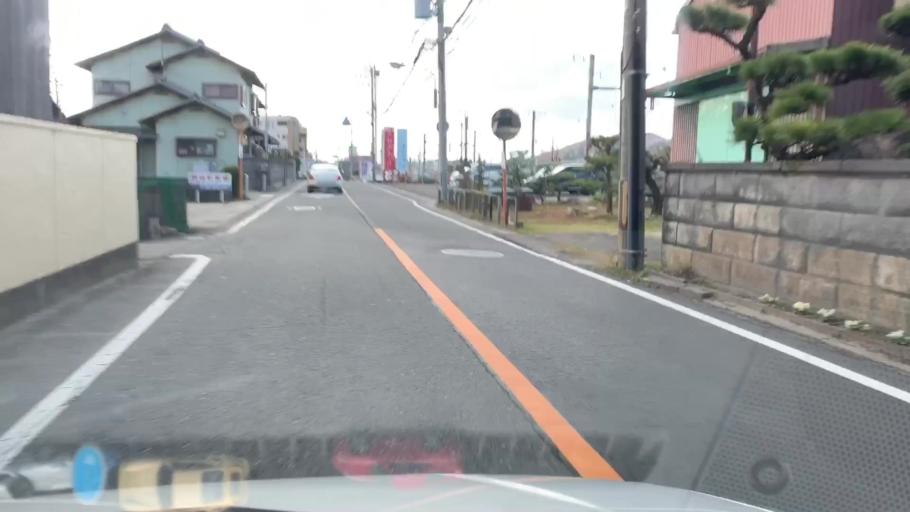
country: JP
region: Wakayama
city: Iwade
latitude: 34.2700
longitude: 135.2515
